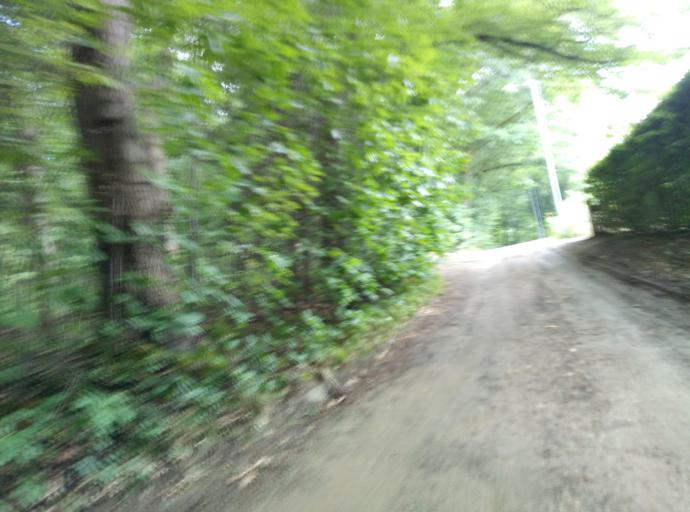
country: BE
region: Flanders
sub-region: Provincie Vlaams-Brabant
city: Holsbeek
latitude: 50.9085
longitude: 4.7368
